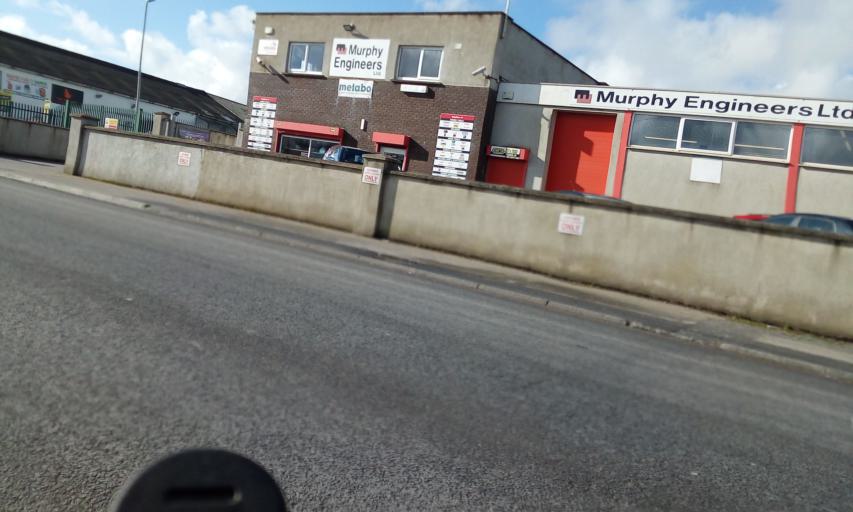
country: IE
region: Leinster
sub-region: Kilkenny
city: Kilkenny
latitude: 52.6560
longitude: -7.2321
